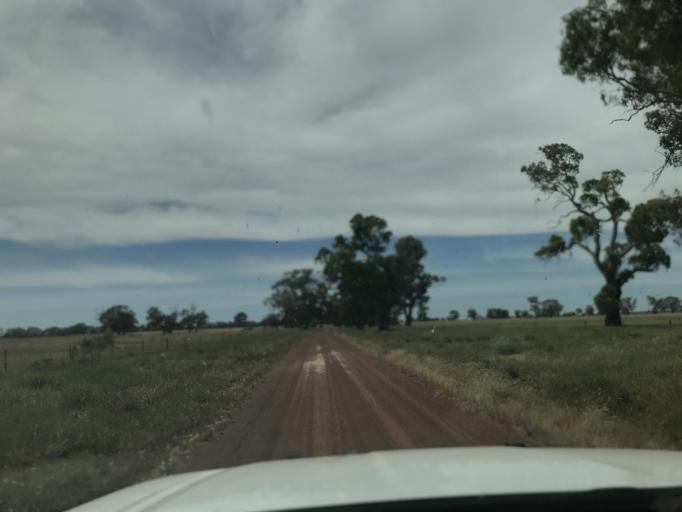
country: AU
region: South Australia
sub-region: Wattle Range
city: Penola
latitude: -37.0088
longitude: 141.4703
